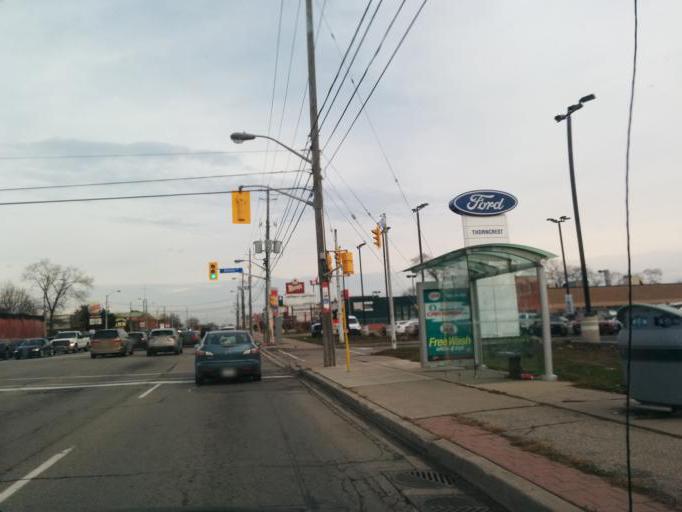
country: CA
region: Ontario
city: Etobicoke
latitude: 43.6176
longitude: -79.5413
